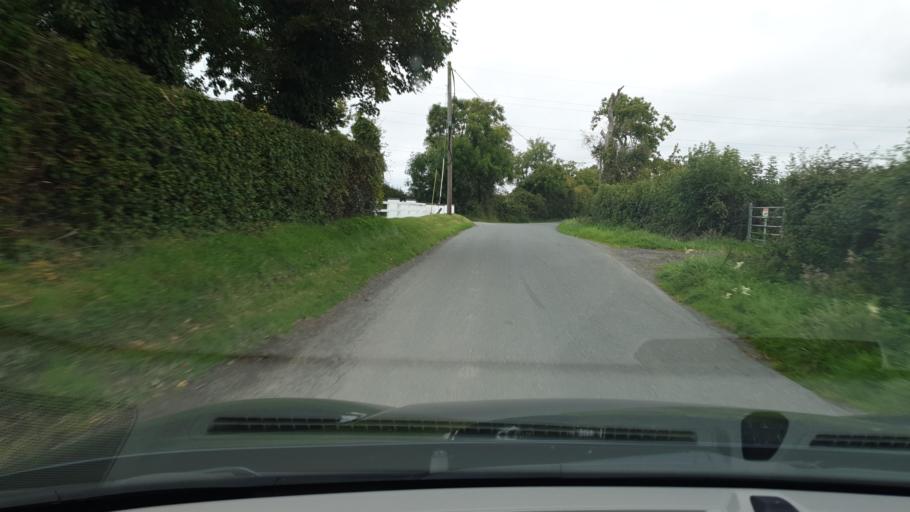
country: IE
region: Leinster
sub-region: An Mhi
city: Ratoath
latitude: 53.4840
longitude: -6.5020
